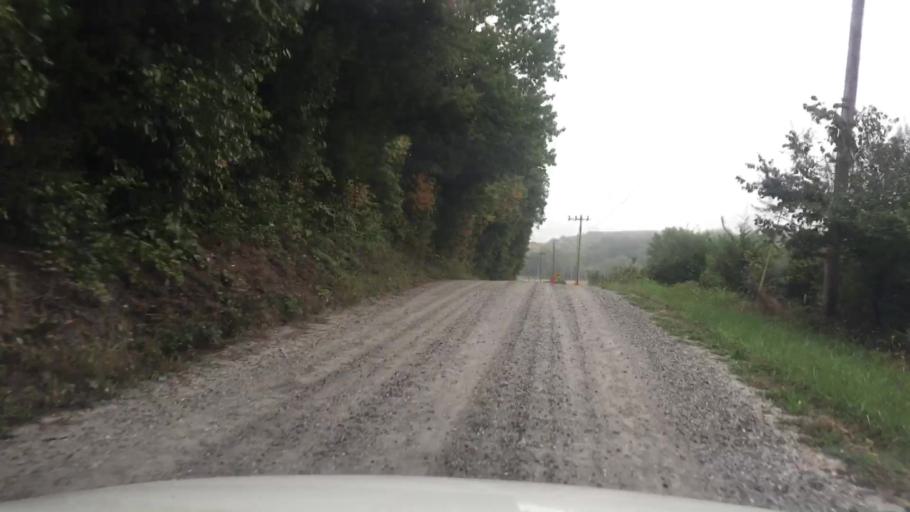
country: US
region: Missouri
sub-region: Boone County
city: Ashland
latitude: 38.8250
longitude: -92.3310
